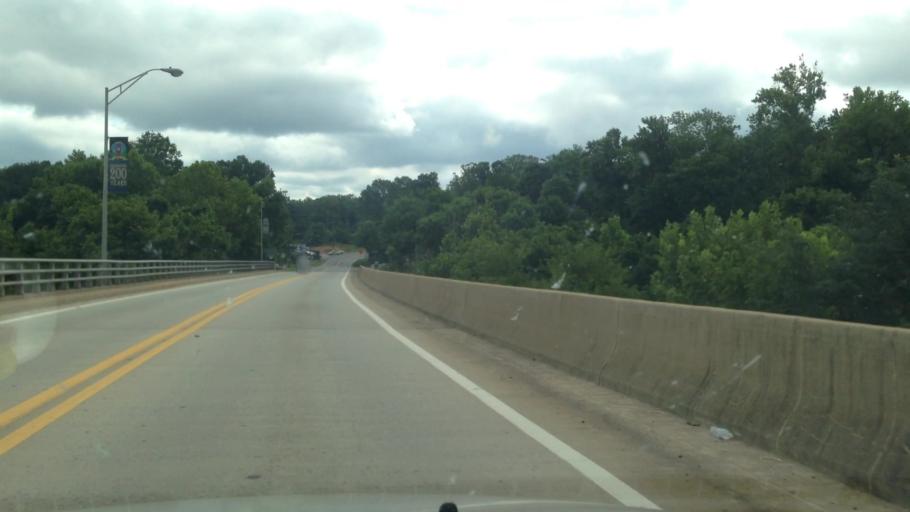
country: US
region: North Carolina
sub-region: Rockingham County
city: Madison
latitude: 36.3852
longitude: -79.9552
